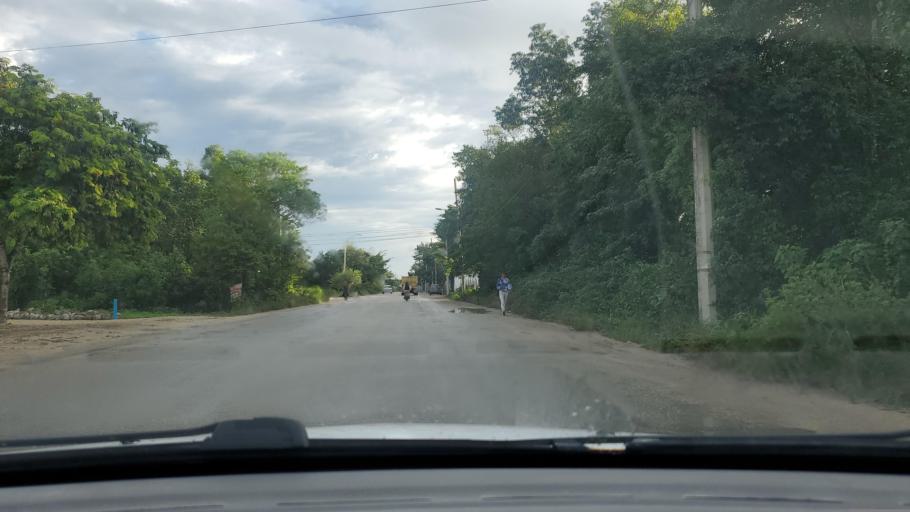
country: MX
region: Quintana Roo
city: Tulum
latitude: 20.2096
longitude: -87.4784
